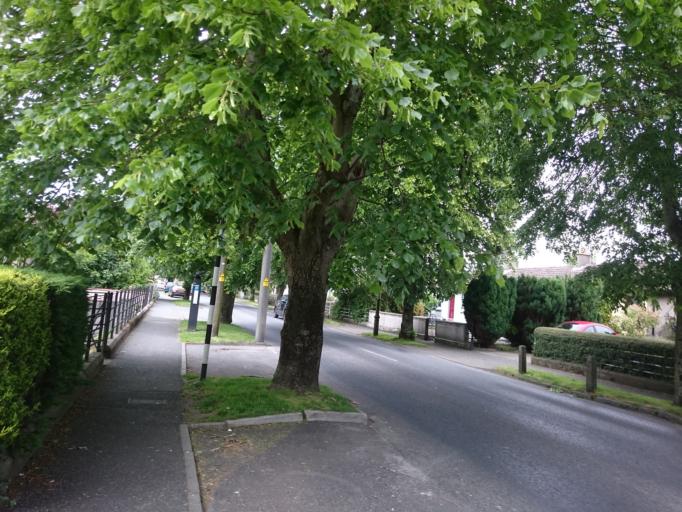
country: IE
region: Leinster
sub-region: Kilkenny
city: Kilkenny
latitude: 52.6500
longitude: -7.2602
